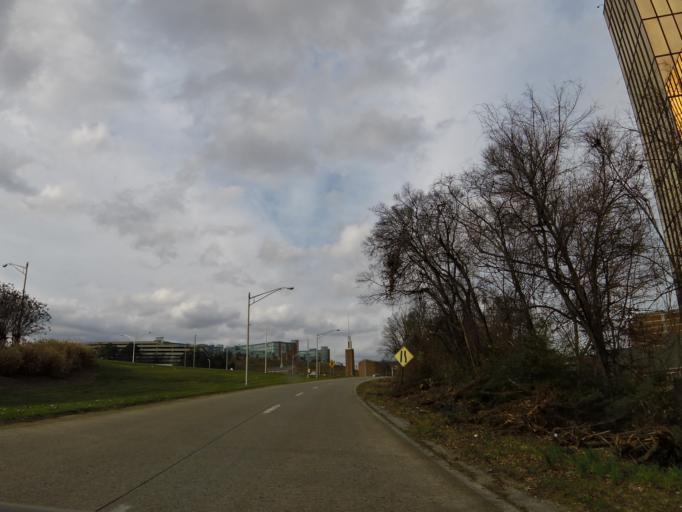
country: US
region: Tennessee
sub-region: Hamilton County
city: Chattanooga
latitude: 35.0468
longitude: -85.3135
